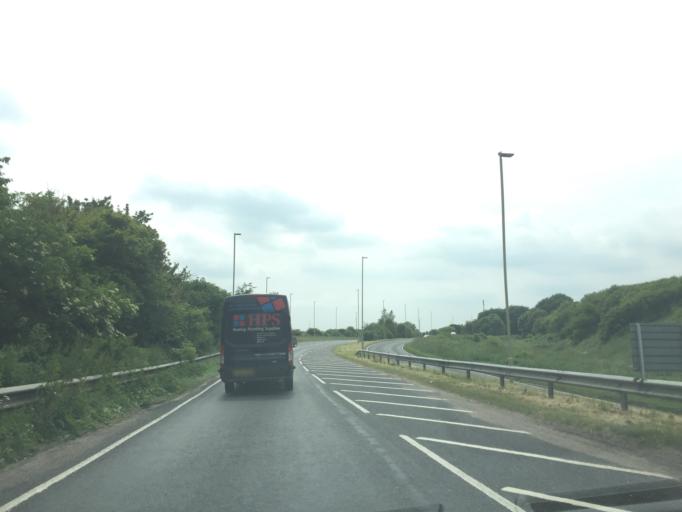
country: GB
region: England
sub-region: Hampshire
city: Kings Worthy
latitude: 51.0596
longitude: -1.2607
